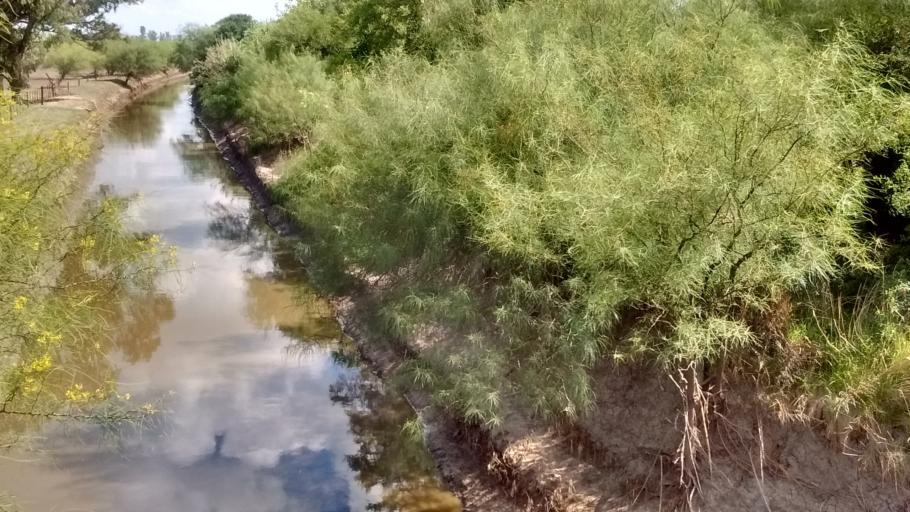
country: AR
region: Cordoba
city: General Roca
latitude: -32.7341
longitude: -61.8385
